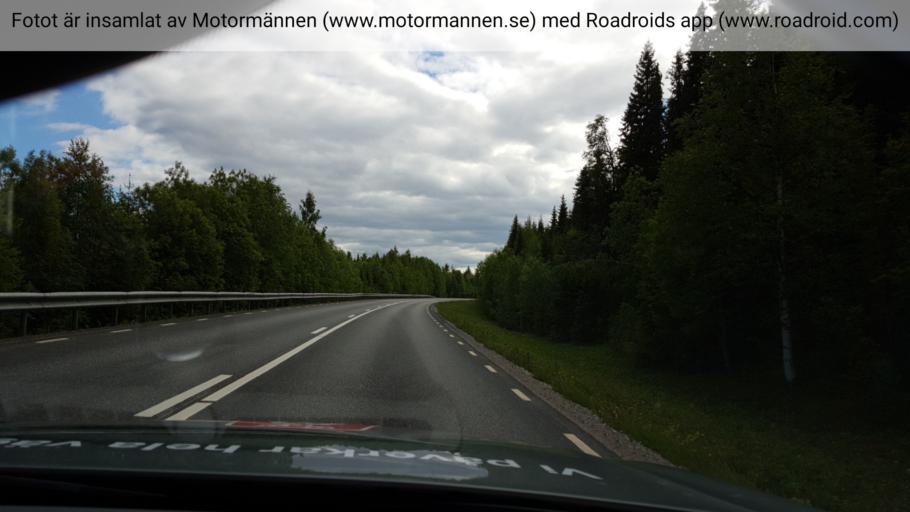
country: SE
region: Jaemtland
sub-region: Stroemsunds Kommun
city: Stroemsund
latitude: 64.0870
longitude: 15.5683
